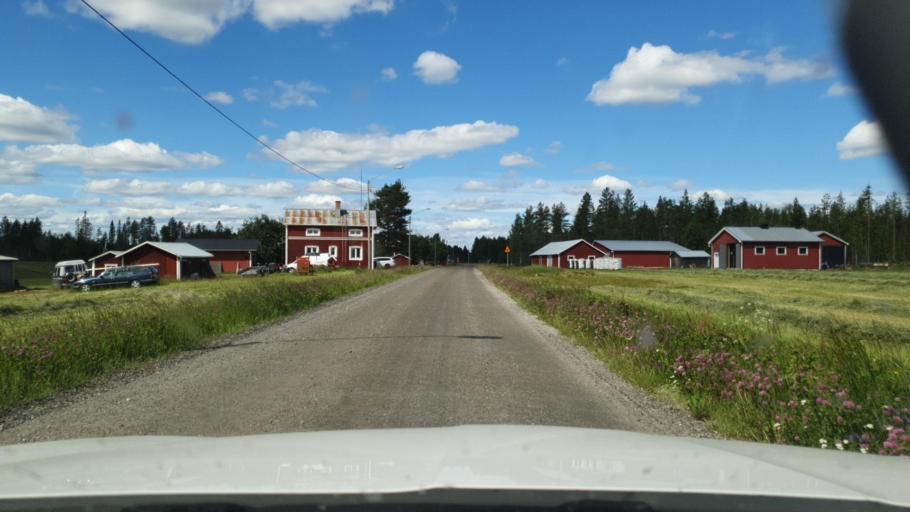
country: SE
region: Vaesterbotten
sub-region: Skelleftea Kommun
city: Backa
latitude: 65.1835
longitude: 21.0664
